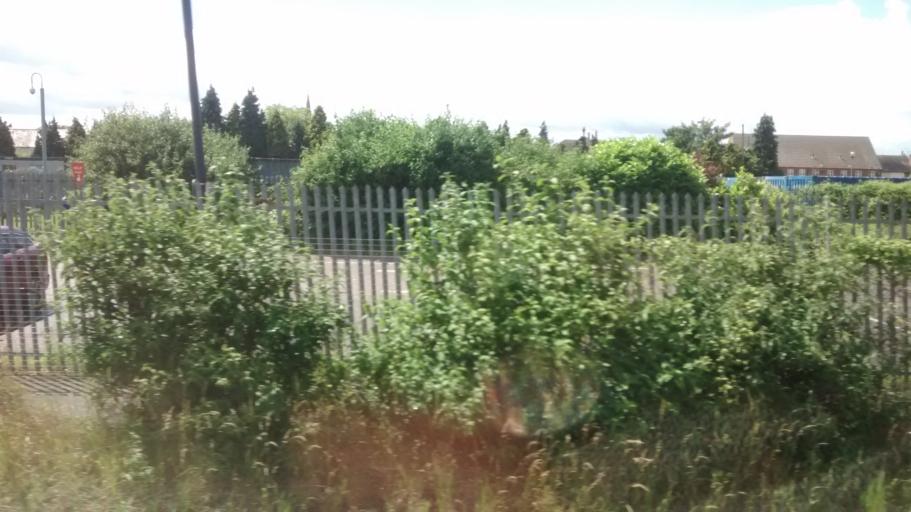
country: GB
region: England
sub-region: Nottinghamshire
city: Newark on Trent
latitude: 53.0800
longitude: -0.7987
